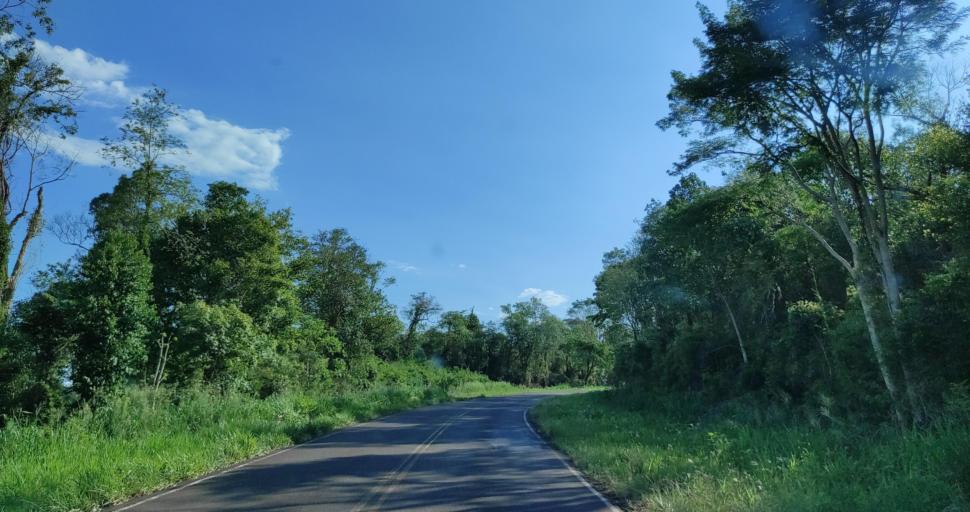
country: AR
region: Misiones
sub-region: Departamento de Eldorado
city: Eldorado
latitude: -26.3742
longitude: -54.3239
